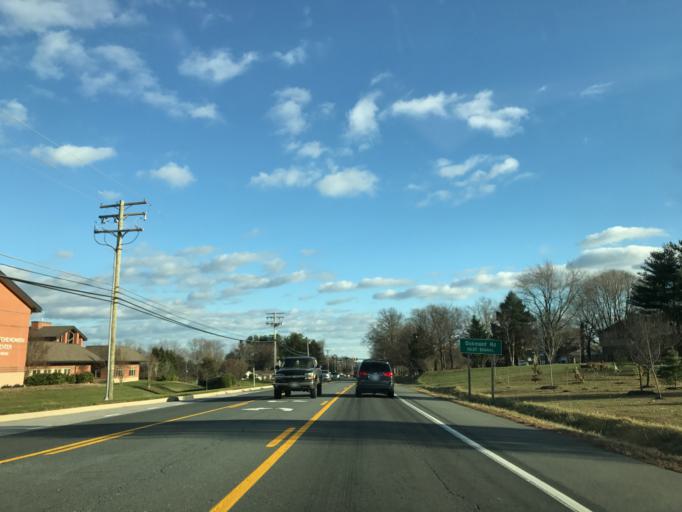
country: US
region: Maryland
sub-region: Harford County
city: Fallston
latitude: 39.5278
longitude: -76.4356
